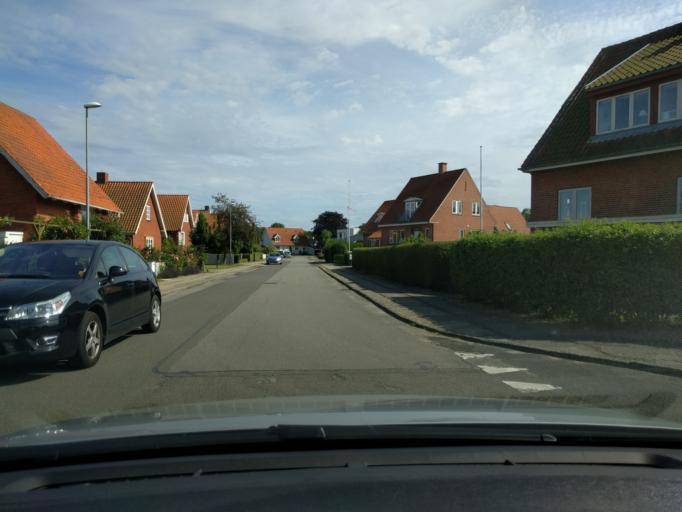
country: DK
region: South Denmark
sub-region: Kerteminde Kommune
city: Kerteminde
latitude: 55.4473
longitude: 10.6647
